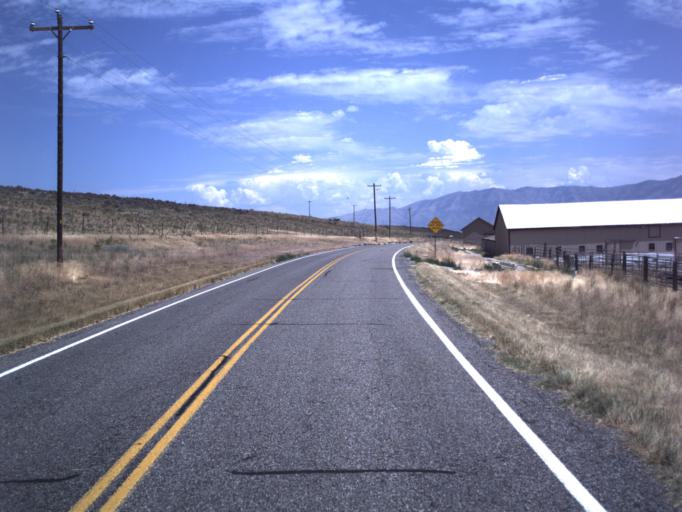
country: US
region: Utah
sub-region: Box Elder County
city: Tremonton
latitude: 41.6241
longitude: -112.3461
